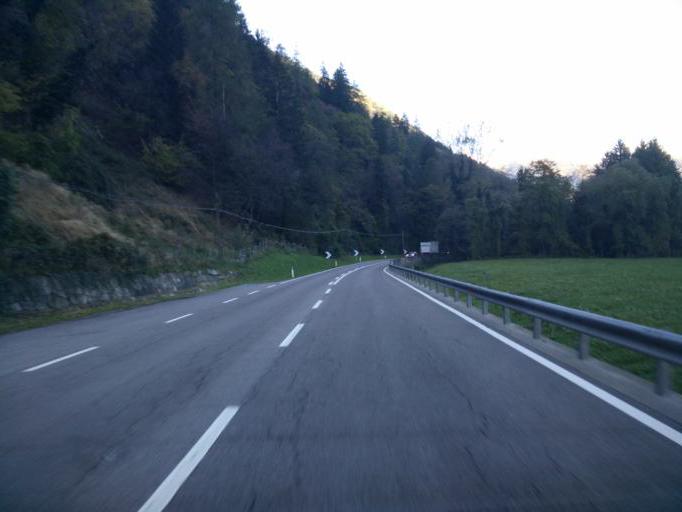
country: IT
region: Trentino-Alto Adige
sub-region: Bolzano
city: San Martino in Passiria
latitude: 46.7569
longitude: 11.2070
